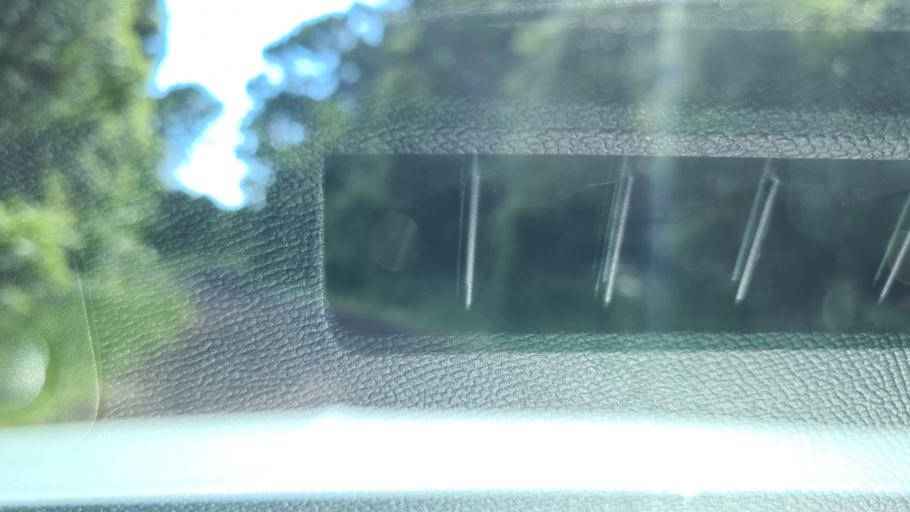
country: PT
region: Azores
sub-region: Sao Roque do Pico
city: Sao Roque do Pico
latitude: 38.4121
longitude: -28.2974
